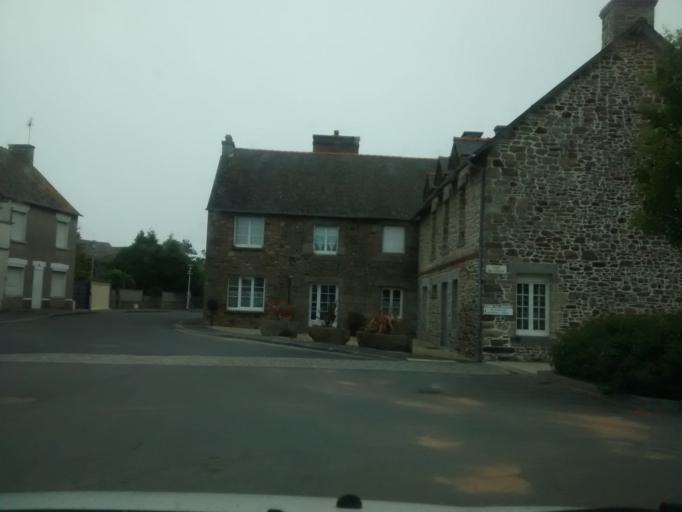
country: FR
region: Brittany
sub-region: Departement d'Ille-et-Vilaine
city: Cherrueix
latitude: 48.6056
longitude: -1.7105
